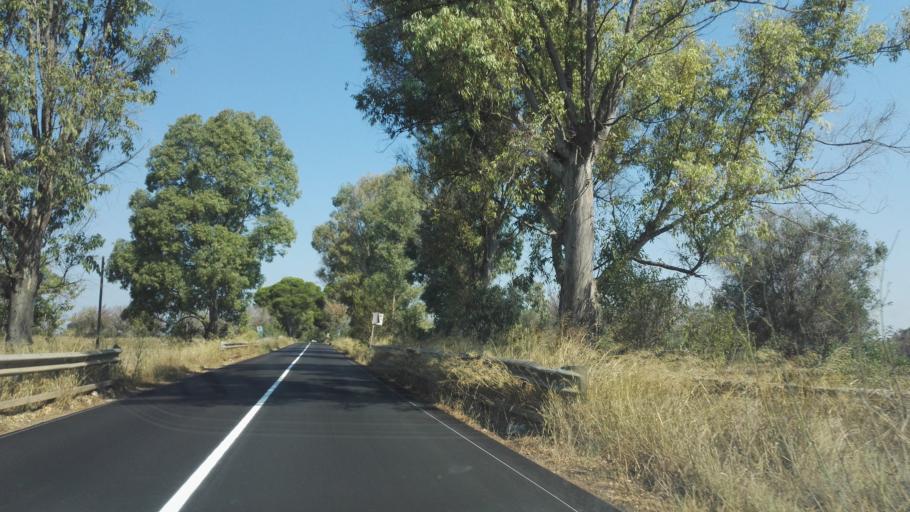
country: IT
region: Apulia
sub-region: Provincia di Lecce
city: Nardo
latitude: 40.1954
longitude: 17.9631
